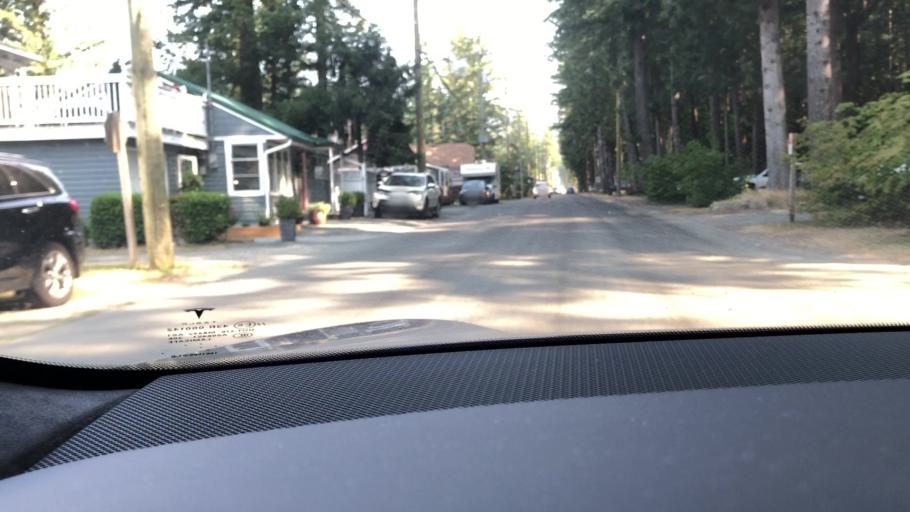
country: CA
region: British Columbia
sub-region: Fraser Valley Regional District
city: Chilliwack
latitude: 49.0690
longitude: -121.9761
